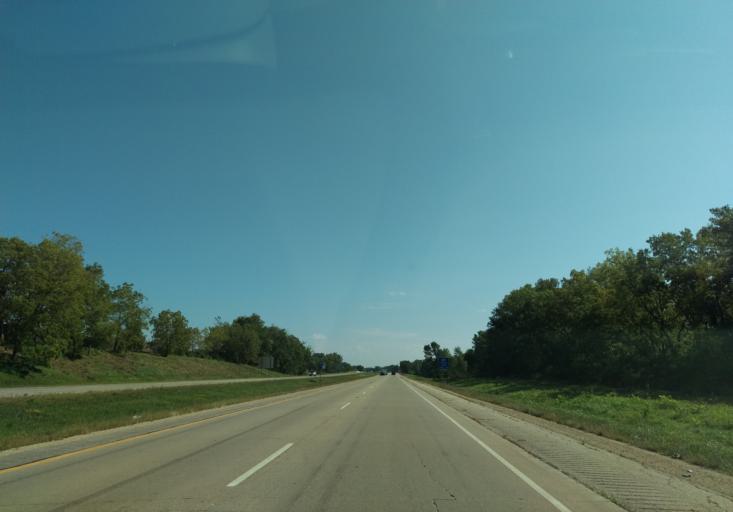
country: US
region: Wisconsin
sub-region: Dane County
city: Verona
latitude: 43.0025
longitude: -89.4895
